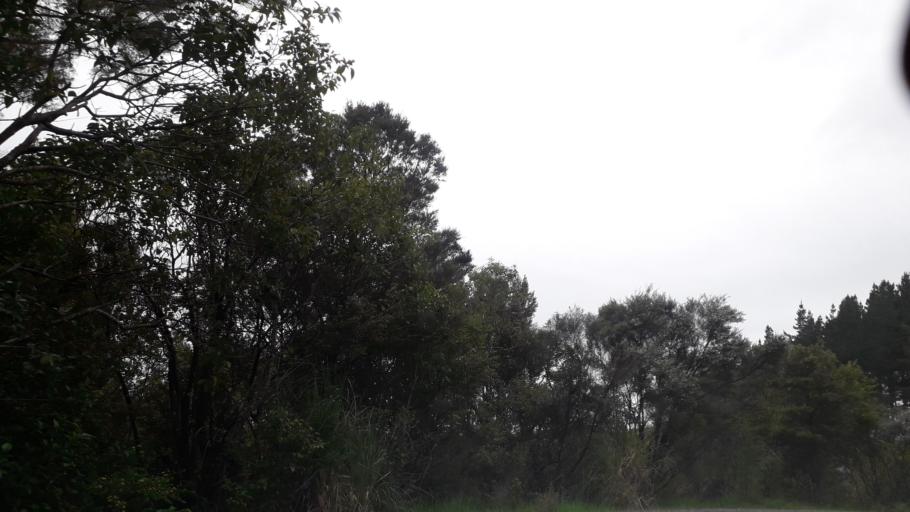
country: NZ
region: Northland
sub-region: Far North District
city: Waimate North
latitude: -35.3043
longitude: 173.5631
